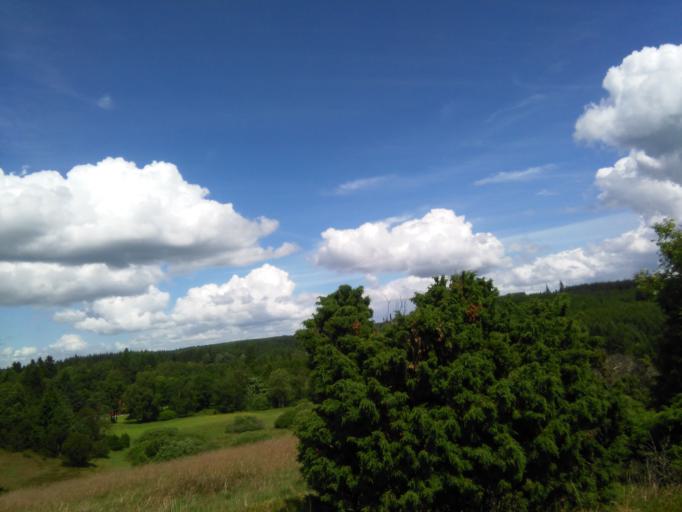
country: DK
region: Central Jutland
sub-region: Silkeborg Kommune
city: Virklund
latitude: 56.0628
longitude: 9.4475
